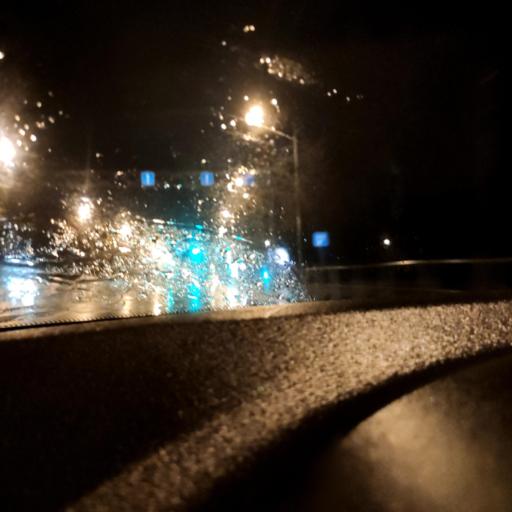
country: RU
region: Samara
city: Petra-Dubrava
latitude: 53.2966
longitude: 50.2449
